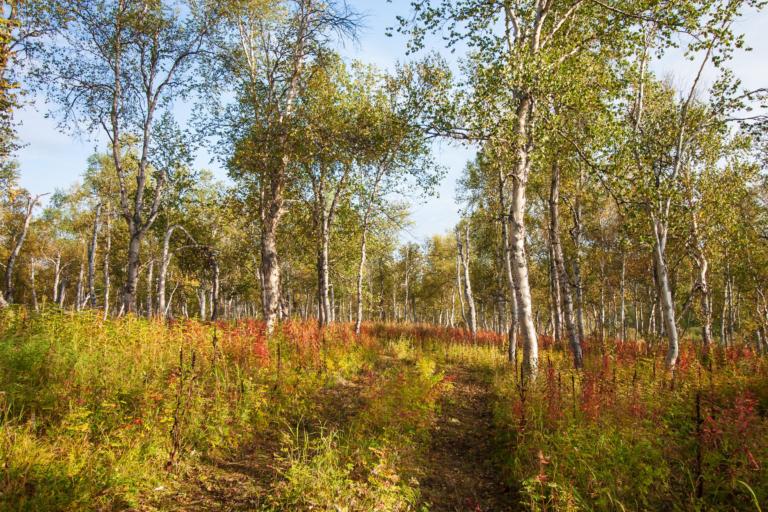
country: RU
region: Kamtsjatka
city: Yelizovo
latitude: 53.7556
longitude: 158.6265
